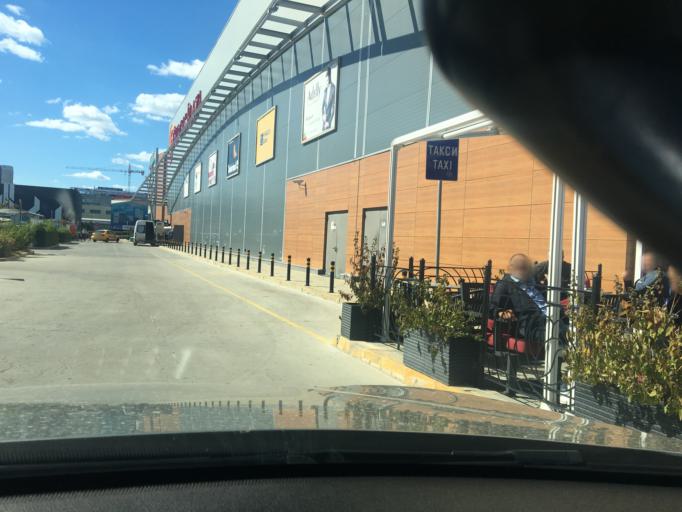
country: BG
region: Burgas
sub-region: Obshtina Burgas
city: Burgas
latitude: 42.5308
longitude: 27.4576
